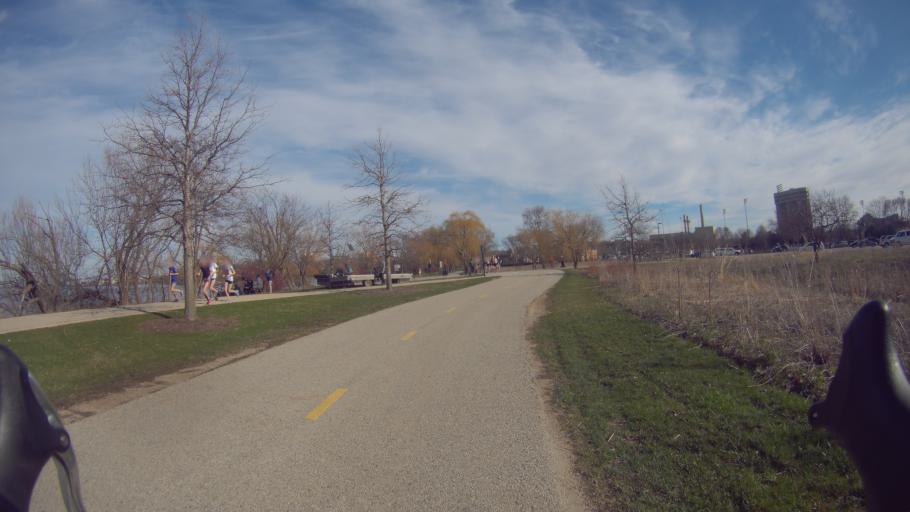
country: US
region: Wisconsin
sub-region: Dane County
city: Shorewood Hills
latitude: 43.0805
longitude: -89.4256
